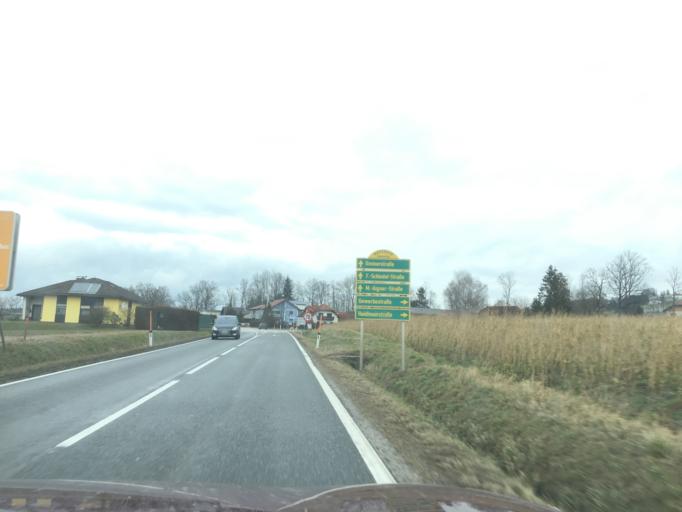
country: AT
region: Upper Austria
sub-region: Politischer Bezirk Kirchdorf an der Krems
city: Micheldorf in Oberoesterreich
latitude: 47.9596
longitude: 14.1283
